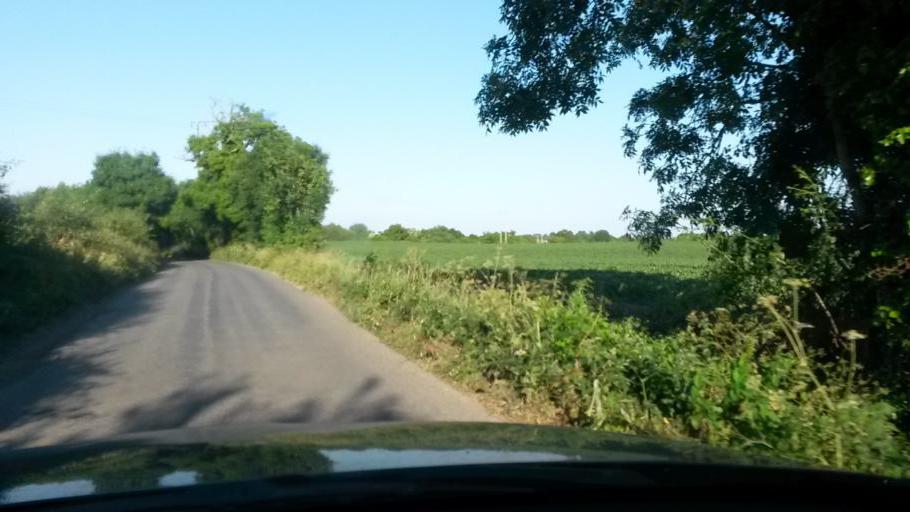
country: IE
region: Leinster
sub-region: Fingal County
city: Swords
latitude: 53.4908
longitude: -6.2904
